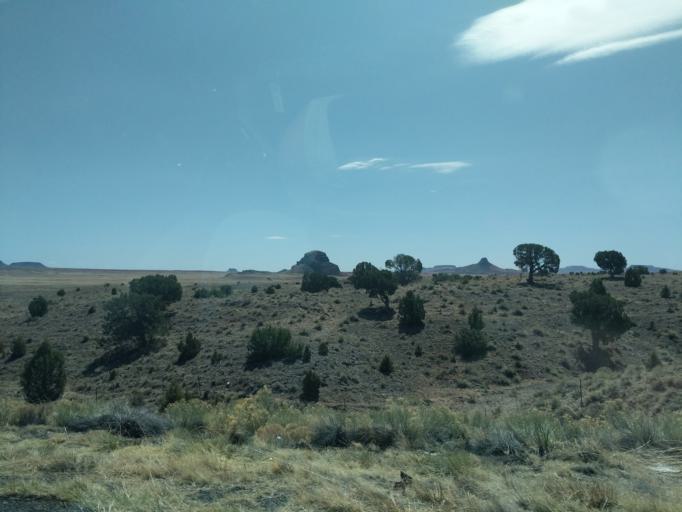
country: US
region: Arizona
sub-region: Navajo County
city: Dilkon
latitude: 35.3939
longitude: -110.0820
